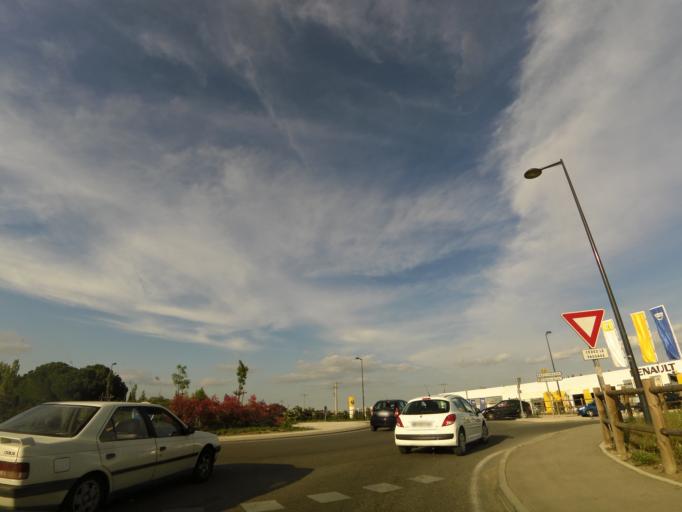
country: FR
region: Languedoc-Roussillon
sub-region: Departement de l'Herault
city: Lunel
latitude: 43.6725
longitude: 4.1475
